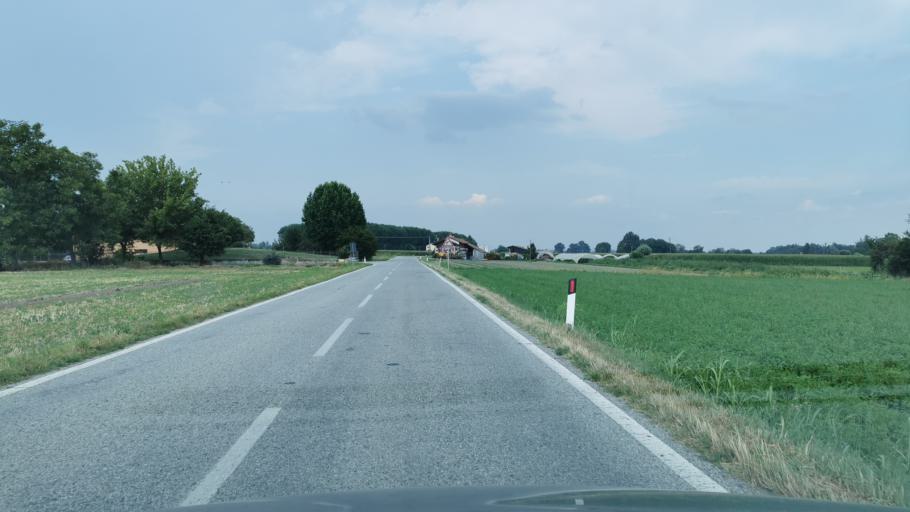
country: IT
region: Piedmont
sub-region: Provincia di Cuneo
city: Vottignasco
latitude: 44.5705
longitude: 7.5917
